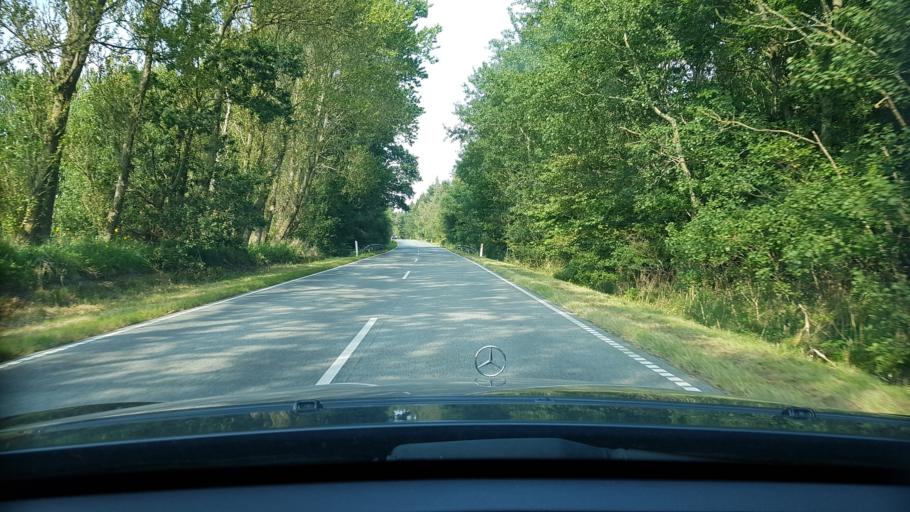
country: DK
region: North Denmark
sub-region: Alborg Kommune
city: Hals
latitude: 56.8949
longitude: 10.2604
